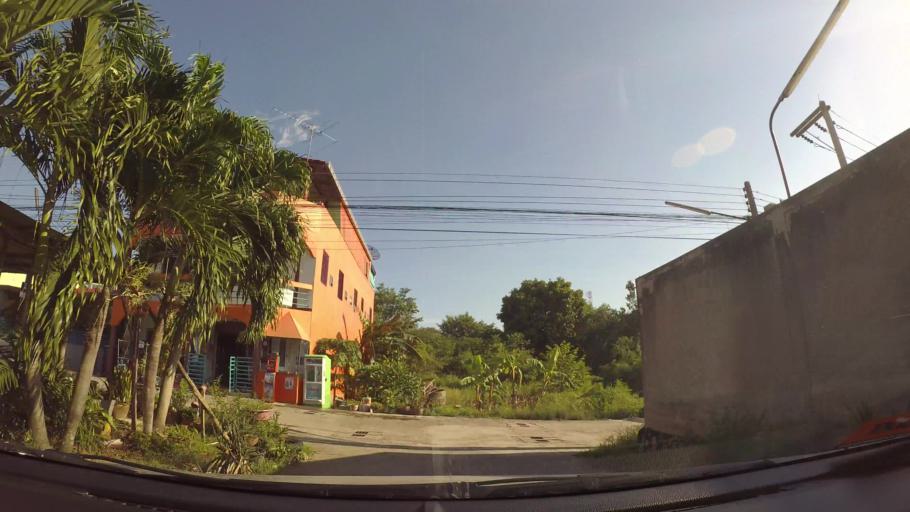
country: TH
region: Chon Buri
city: Si Racha
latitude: 13.1503
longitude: 100.9373
